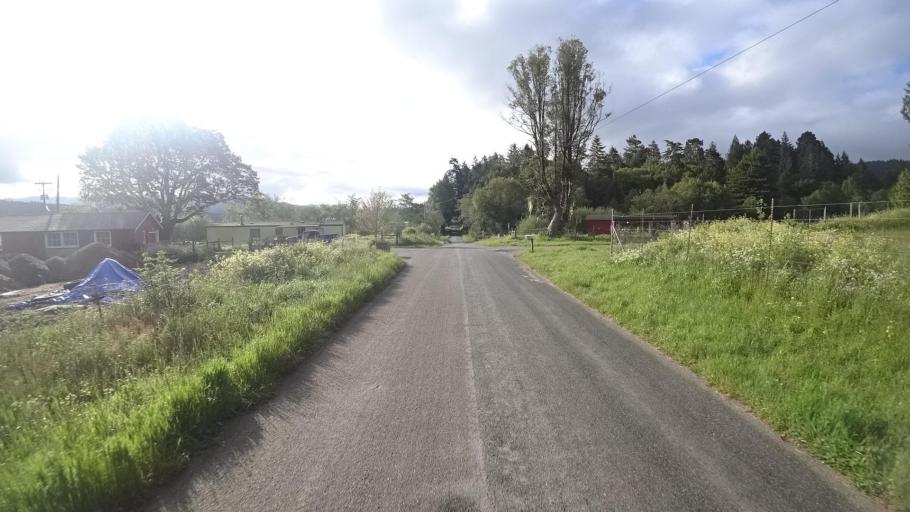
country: US
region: California
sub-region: Humboldt County
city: Blue Lake
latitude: 40.8776
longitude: -124.0133
